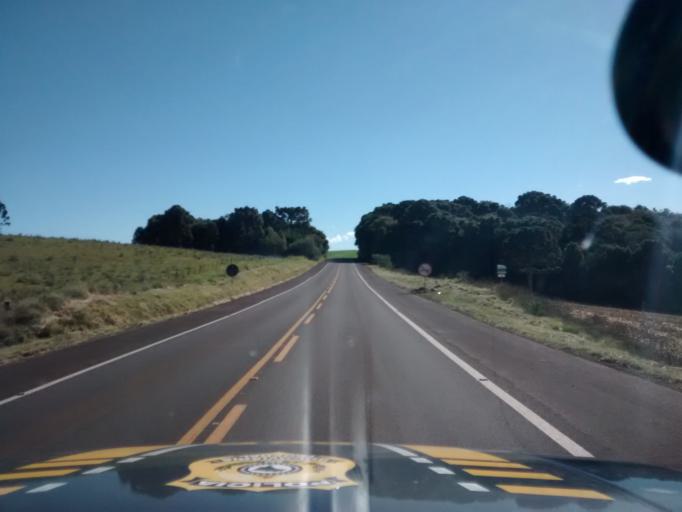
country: BR
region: Rio Grande do Sul
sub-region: Lagoa Vermelha
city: Lagoa Vermelha
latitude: -28.3299
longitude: -51.2821
